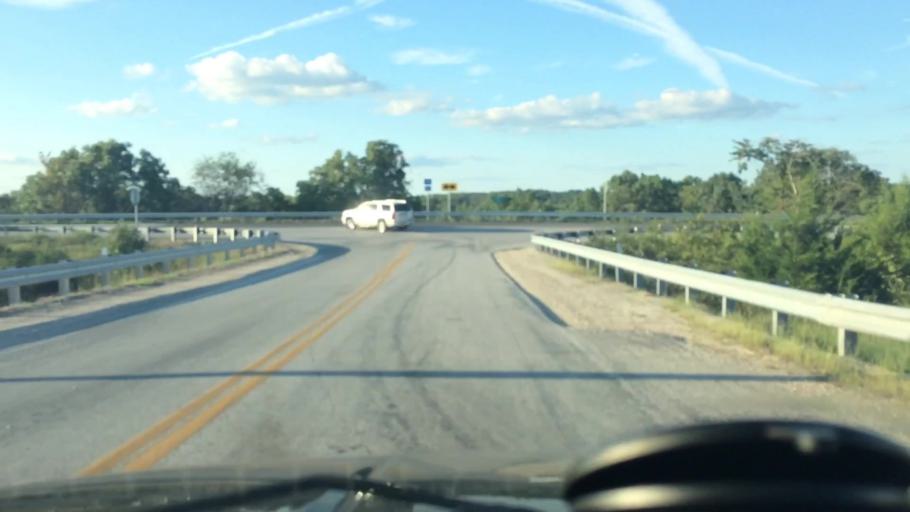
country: US
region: Missouri
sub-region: Webster County
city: Marshfield
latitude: 37.3022
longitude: -92.9994
